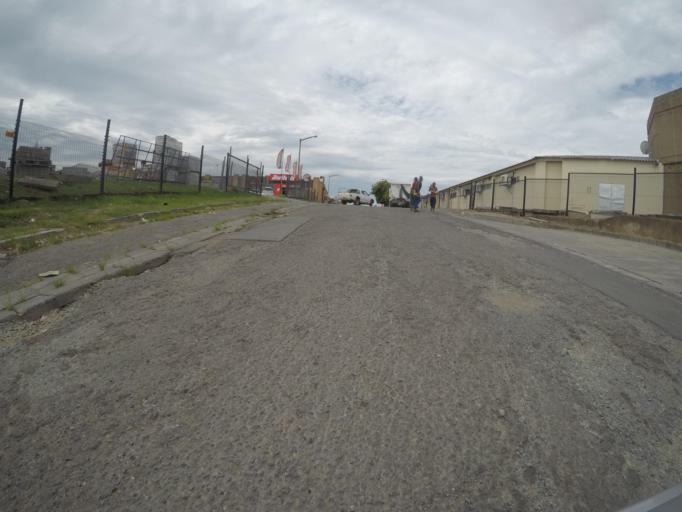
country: ZA
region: Eastern Cape
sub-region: Buffalo City Metropolitan Municipality
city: East London
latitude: -32.9941
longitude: 27.8664
